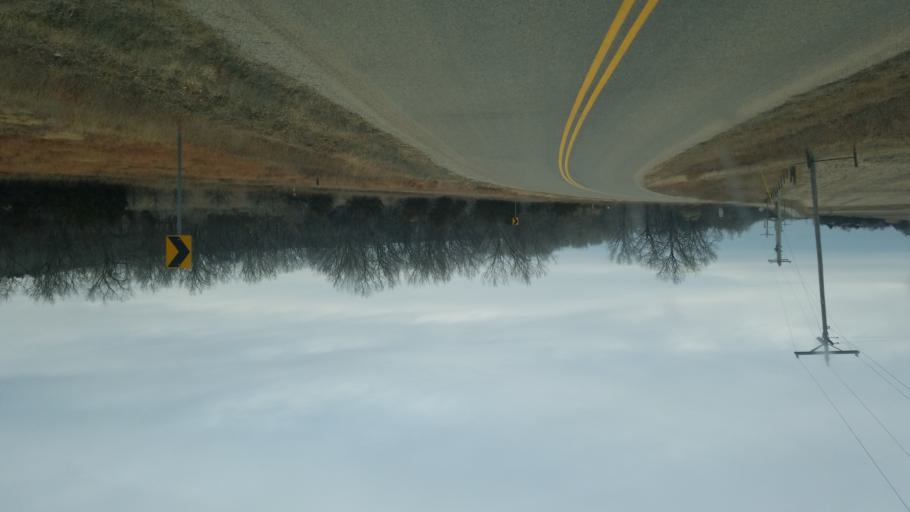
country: US
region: Nebraska
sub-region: Knox County
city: Center
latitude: 42.6185
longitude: -97.8794
